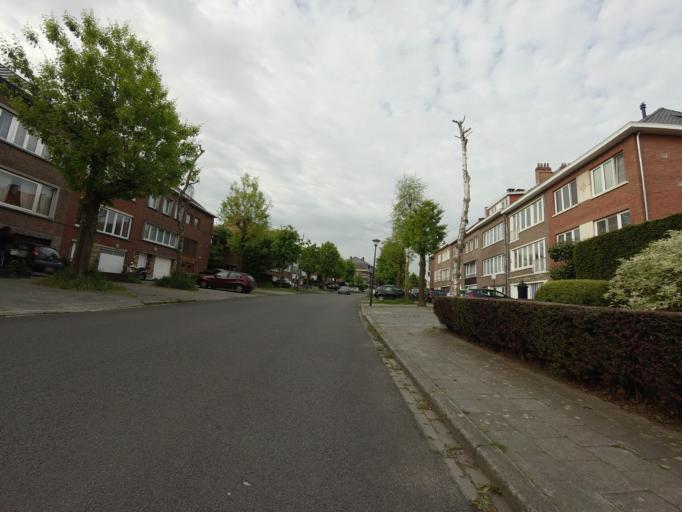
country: BE
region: Flanders
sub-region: Provincie Vlaams-Brabant
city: Grimbergen
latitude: 50.9019
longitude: 4.3684
